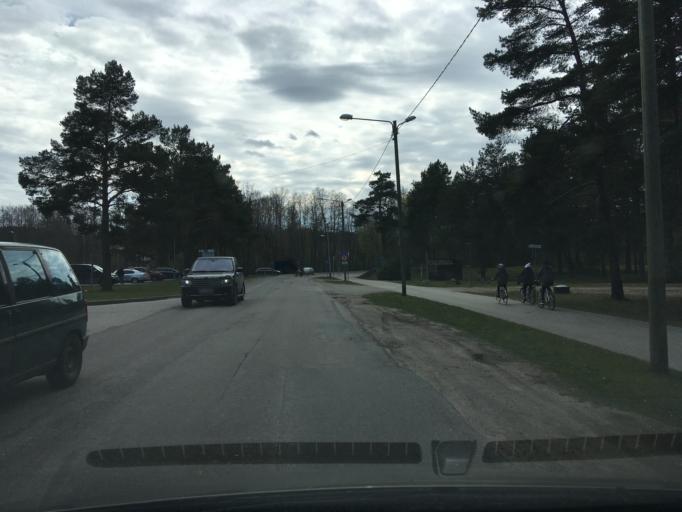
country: EE
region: Harju
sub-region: Tallinna linn
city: Kose
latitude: 59.4747
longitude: 24.9156
